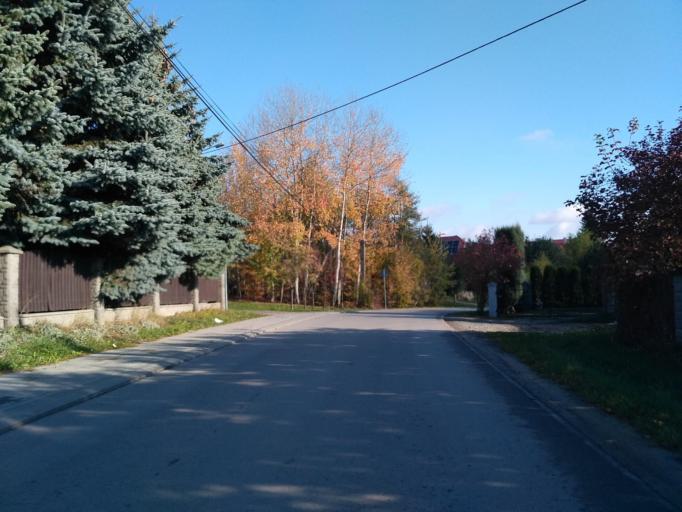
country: PL
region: Subcarpathian Voivodeship
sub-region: Powiat rzeszowski
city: Niechobrz
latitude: 49.9947
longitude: 21.8722
